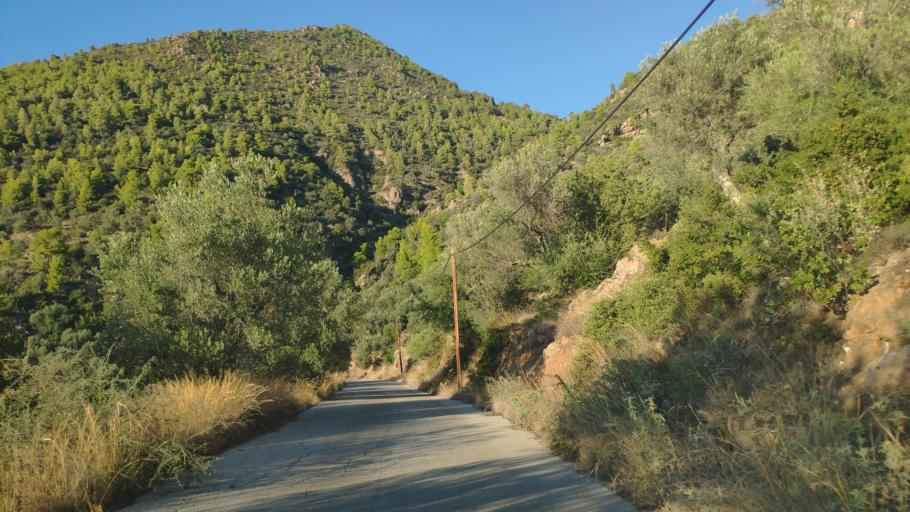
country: GR
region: Attica
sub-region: Nomos Piraios
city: Megalochori
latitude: 37.5985
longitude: 23.3370
